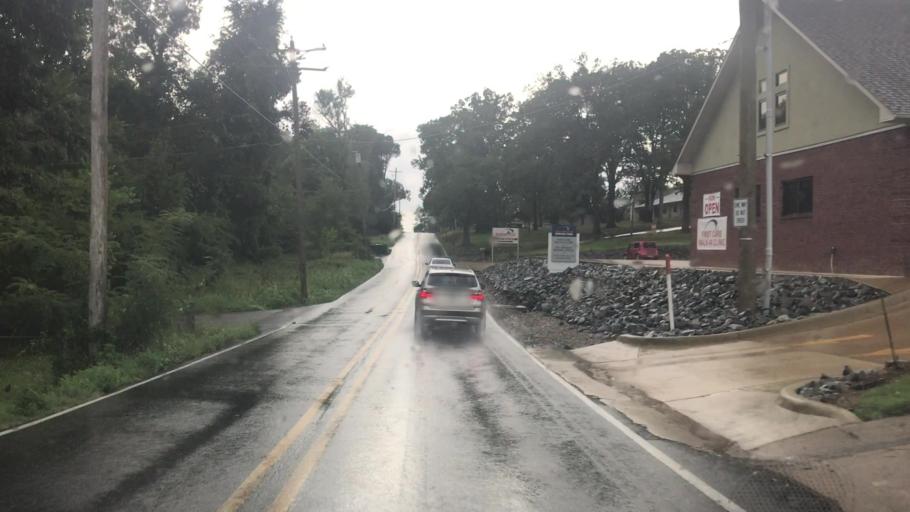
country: US
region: Arkansas
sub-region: Garland County
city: Rockwell
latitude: 34.4671
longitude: -93.1398
